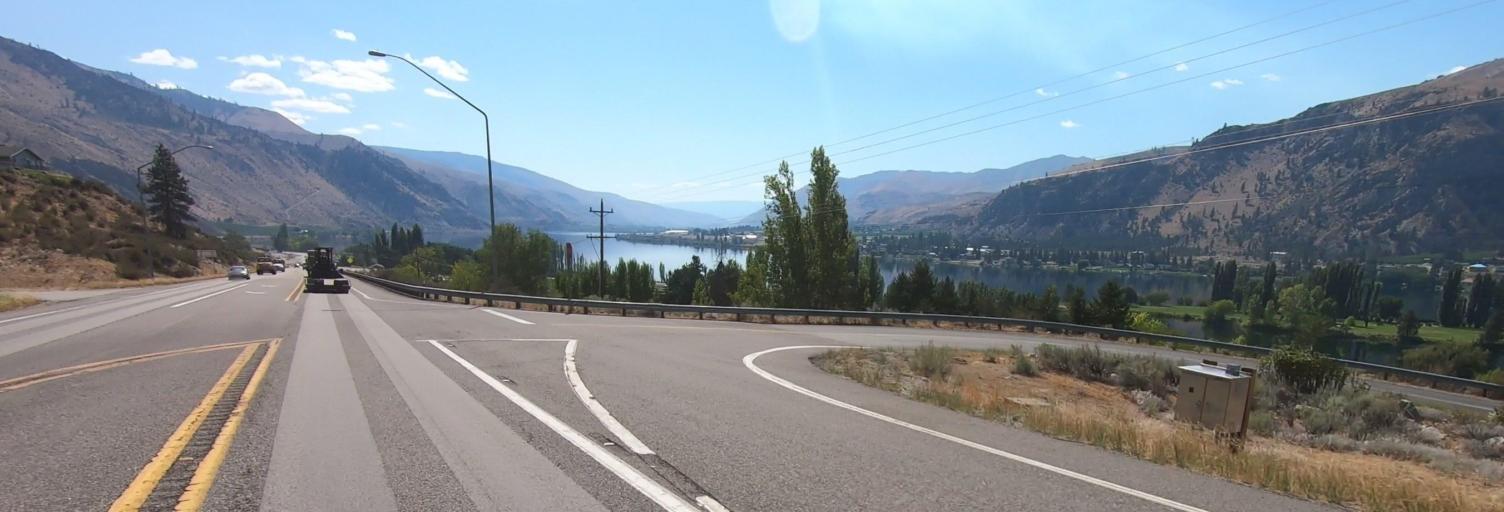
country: US
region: Washington
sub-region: Chelan County
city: Entiat
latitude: 47.7080
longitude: -120.1962
